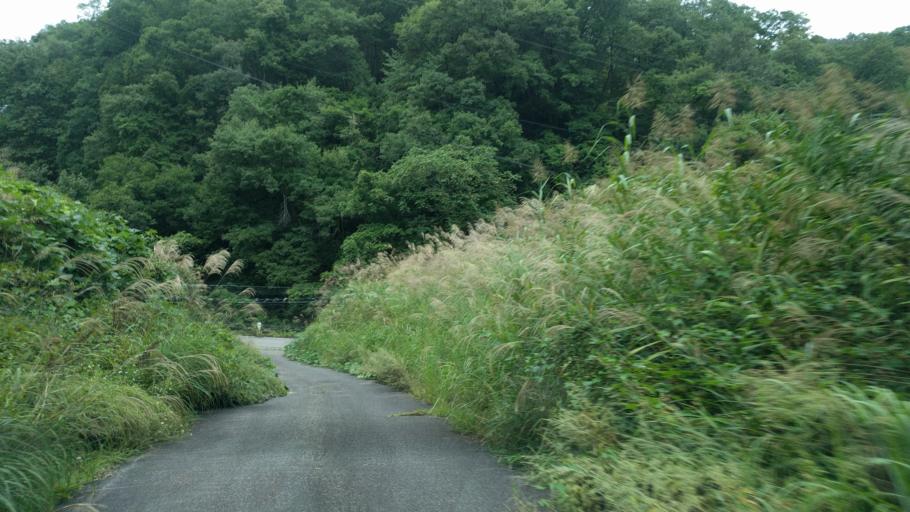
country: JP
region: Fukushima
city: Kitakata
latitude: 37.4798
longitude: 139.7746
